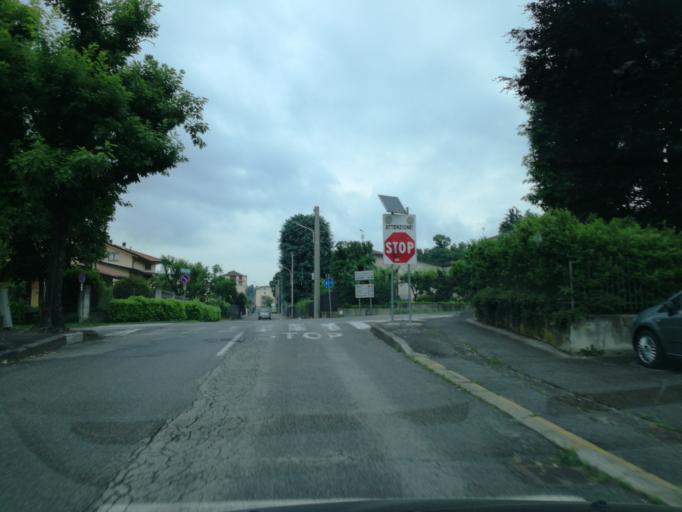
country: IT
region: Lombardy
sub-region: Provincia di Monza e Brianza
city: Carnate
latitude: 45.6500
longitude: 9.3755
